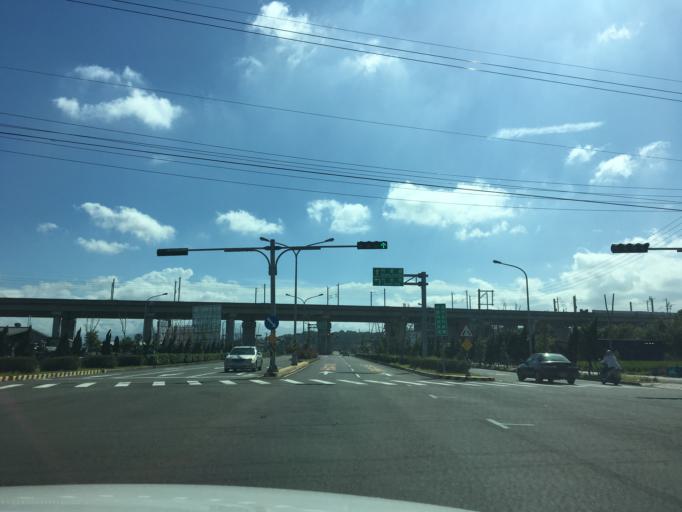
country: TW
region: Taiwan
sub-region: Hsinchu
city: Zhubei
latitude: 24.7865
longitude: 121.0328
